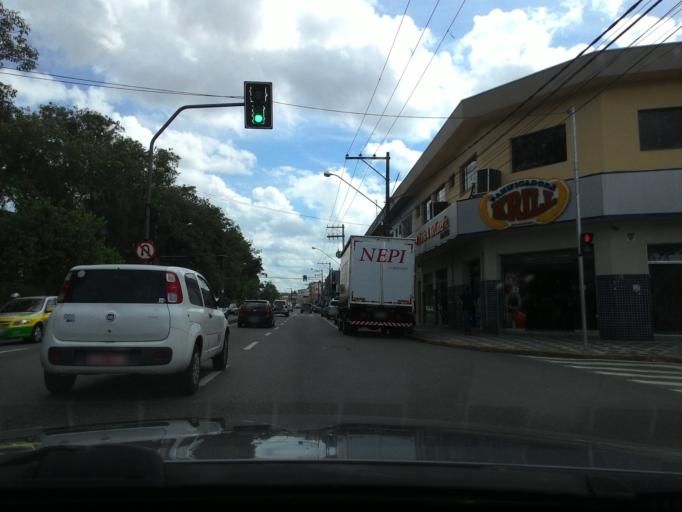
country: BR
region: Sao Paulo
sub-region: Registro
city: Registro
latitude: -24.4969
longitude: -47.8484
